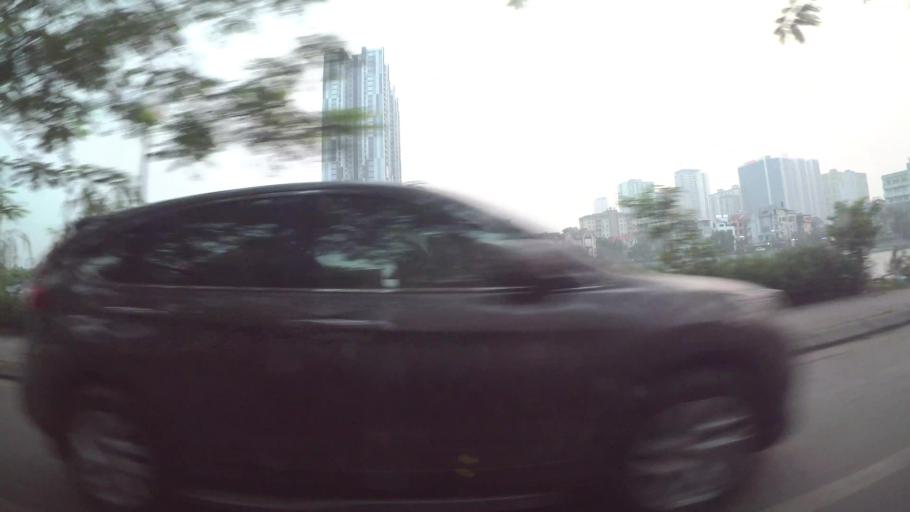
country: VN
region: Ha Noi
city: Ha Dong
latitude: 20.9784
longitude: 105.7915
